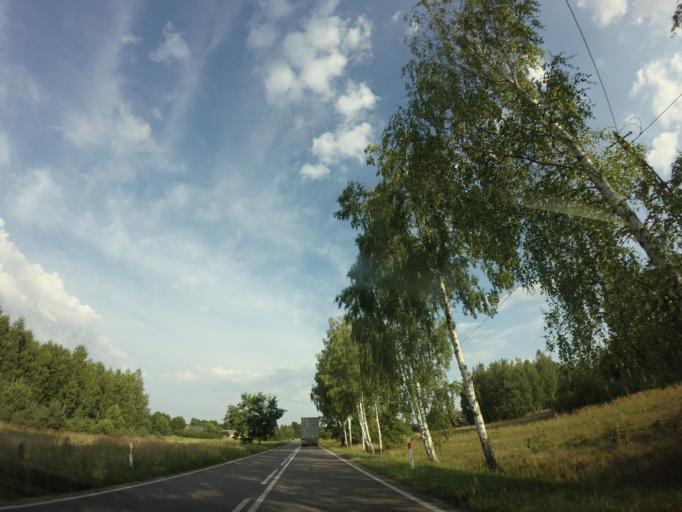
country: PL
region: Lublin Voivodeship
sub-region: Powiat lubartowski
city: Jeziorzany
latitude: 51.5751
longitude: 22.2886
